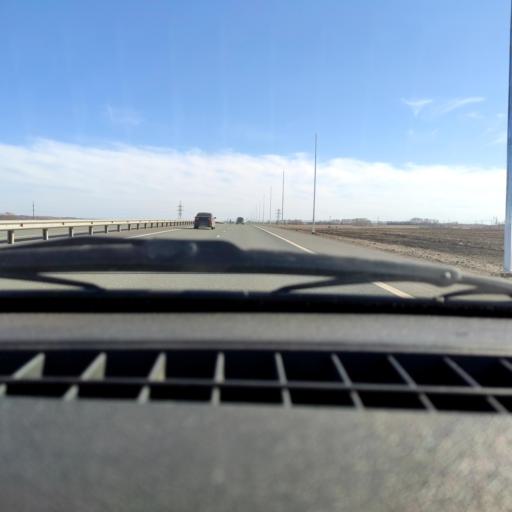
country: RU
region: Bashkortostan
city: Tolbazy
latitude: 54.2780
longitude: 55.8811
